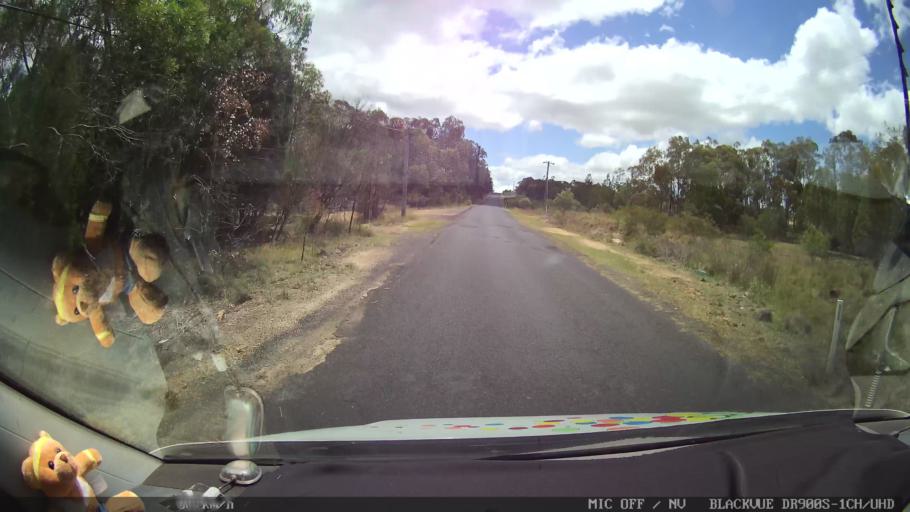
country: AU
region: New South Wales
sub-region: Glen Innes Severn
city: Glen Innes
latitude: -29.4413
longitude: 151.6147
